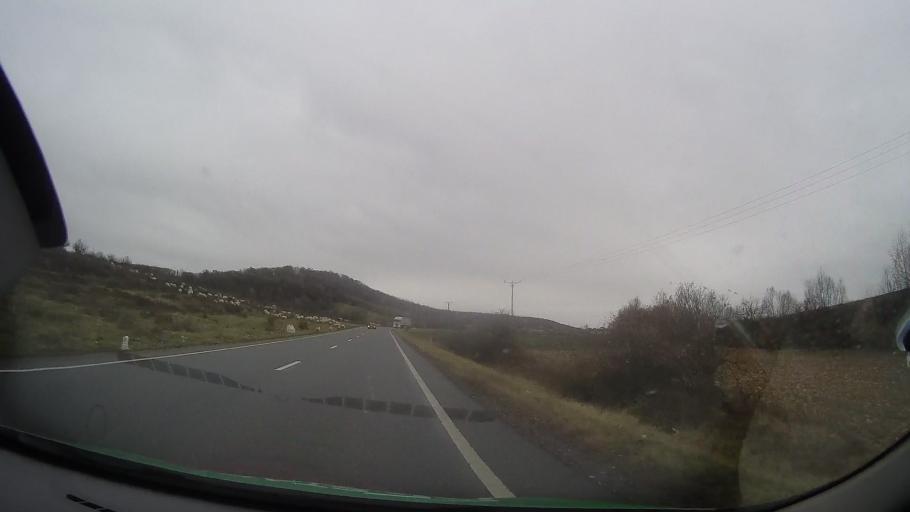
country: RO
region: Mures
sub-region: Comuna Breaza
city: Breaza
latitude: 46.7813
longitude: 24.6540
